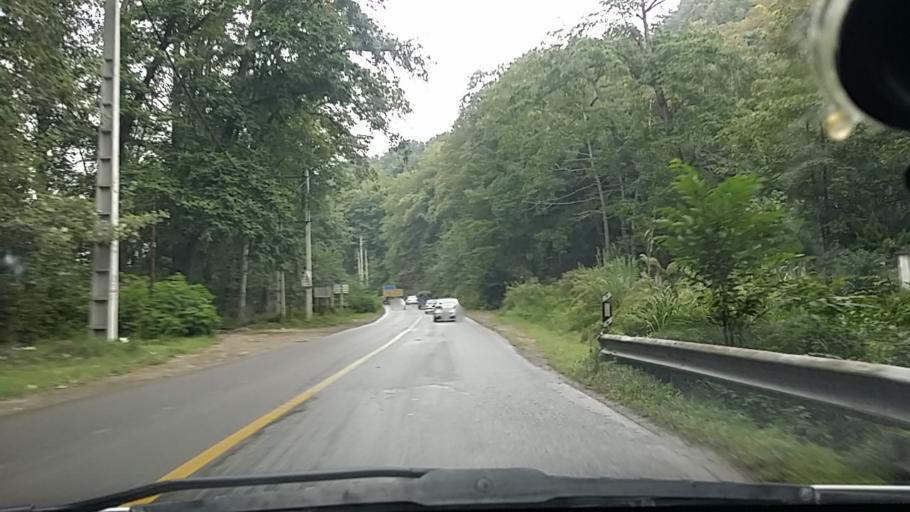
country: IR
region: Mazandaran
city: Chalus
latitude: 36.6174
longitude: 51.3934
